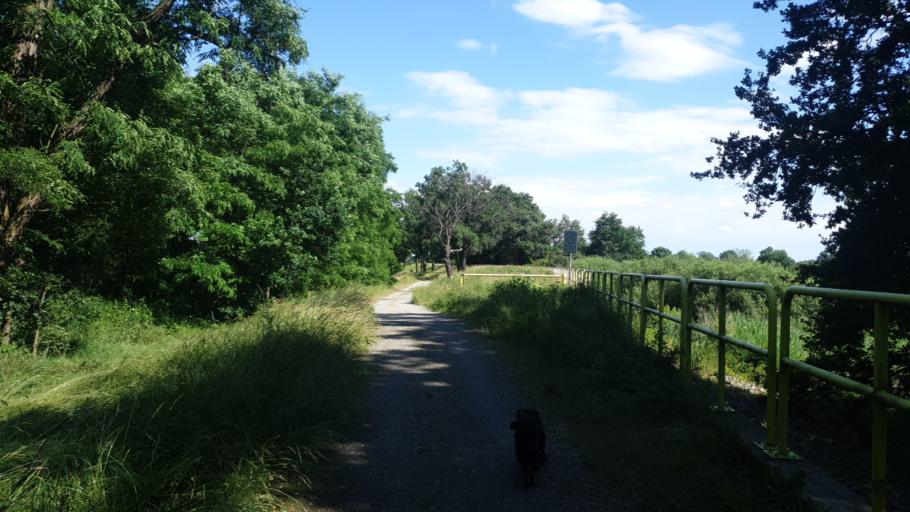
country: PL
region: Lower Silesian Voivodeship
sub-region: Powiat wroclawski
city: Radwanice
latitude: 51.0843
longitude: 17.1184
